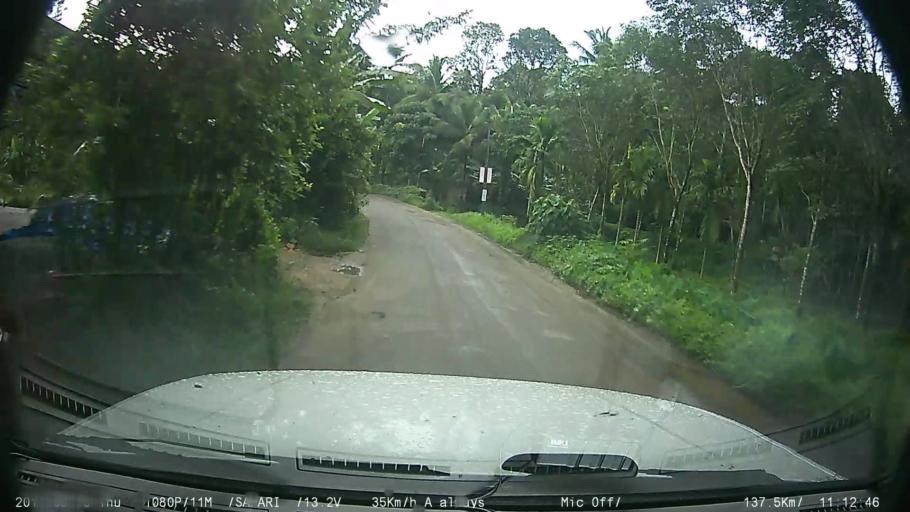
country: IN
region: Kerala
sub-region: Ernakulam
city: Muvattupuzha
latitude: 9.9020
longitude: 76.6042
